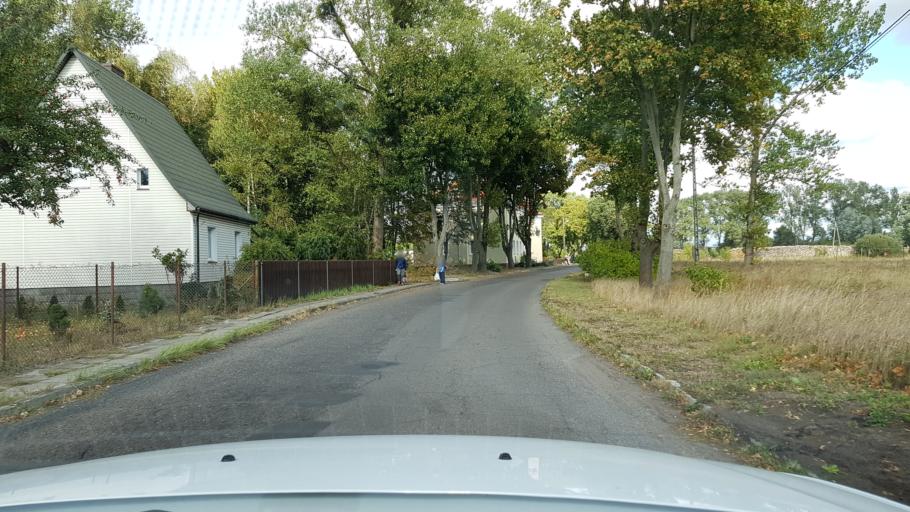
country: PL
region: West Pomeranian Voivodeship
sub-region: Powiat gryfinski
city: Gryfino
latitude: 53.2803
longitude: 14.4973
